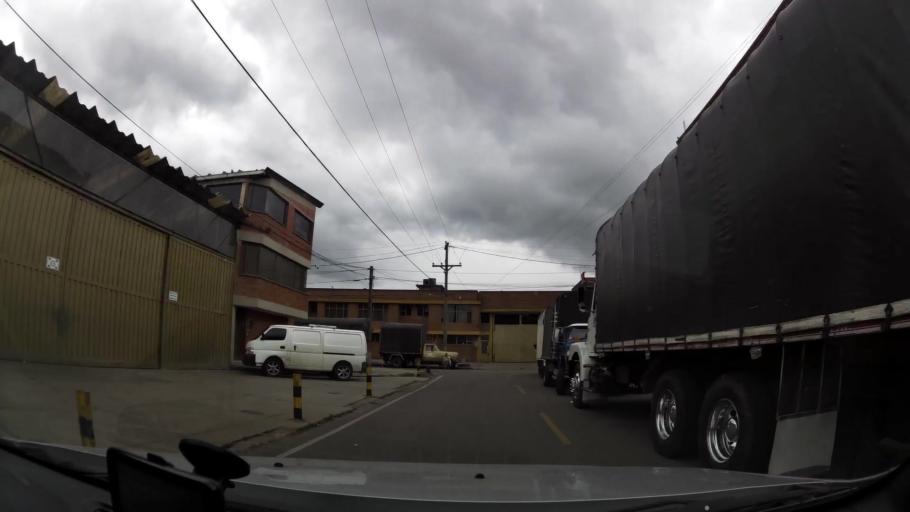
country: CO
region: Bogota D.C.
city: Bogota
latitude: 4.6099
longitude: -74.1038
